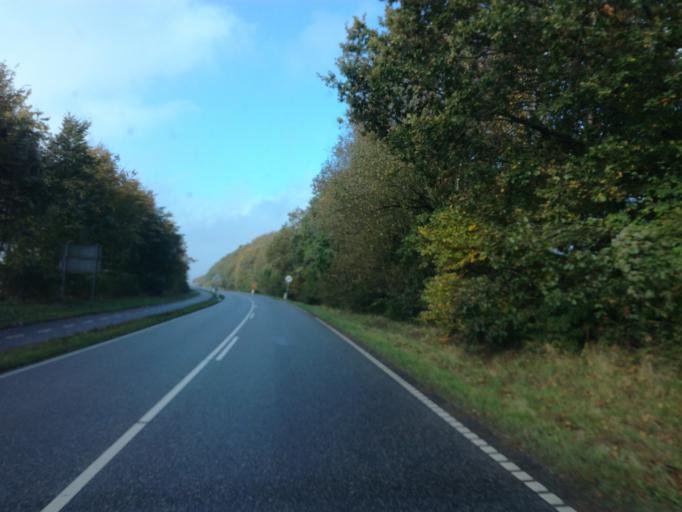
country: DK
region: South Denmark
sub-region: Vejle Kommune
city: Borkop
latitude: 55.6745
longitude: 9.6100
